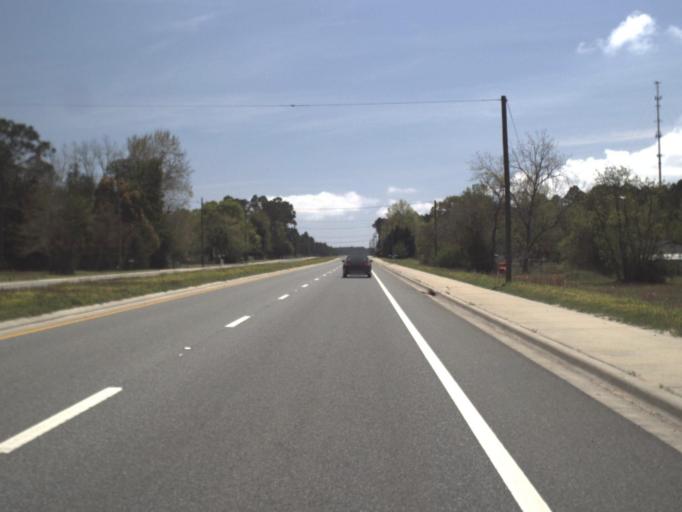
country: US
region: Florida
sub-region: Bay County
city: Laguna Beach
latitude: 30.3271
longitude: -85.8572
